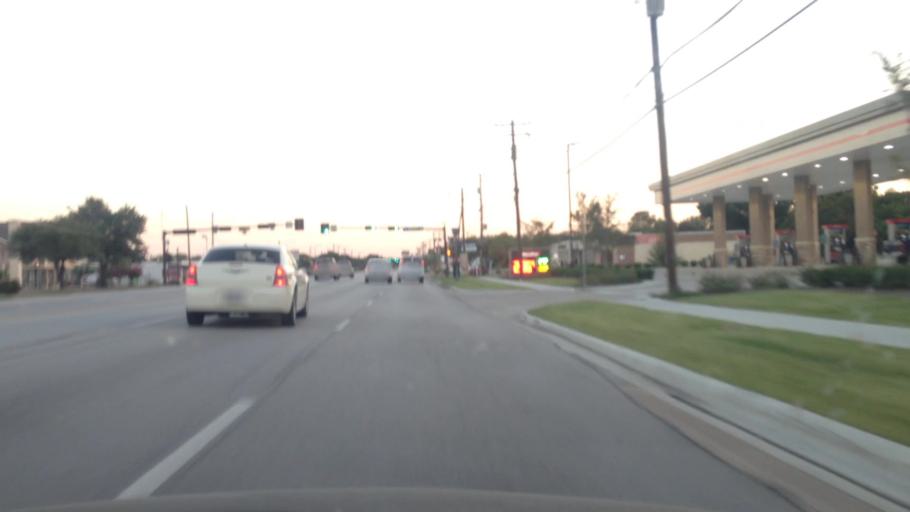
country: US
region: Texas
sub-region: Tarrant County
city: North Richland Hills
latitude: 32.8379
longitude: -97.2142
